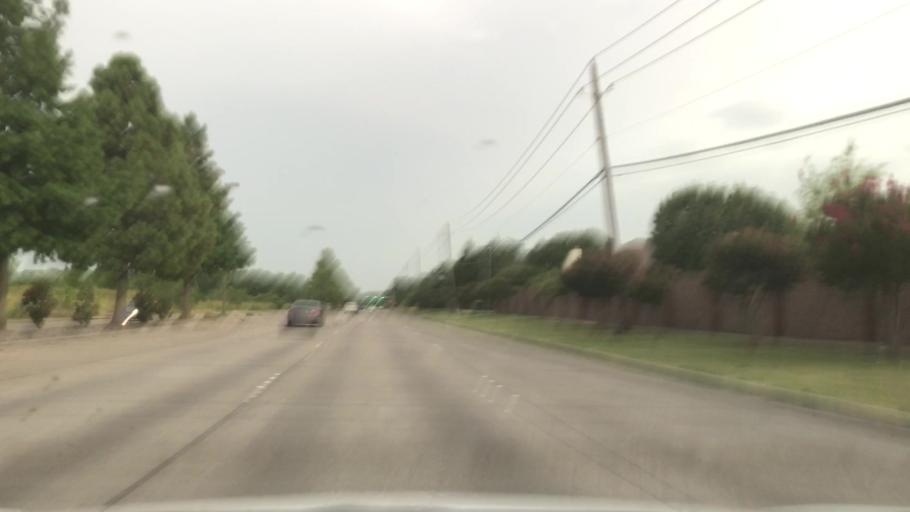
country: US
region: Texas
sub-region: Dallas County
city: Mesquite
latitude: 32.7411
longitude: -96.5759
